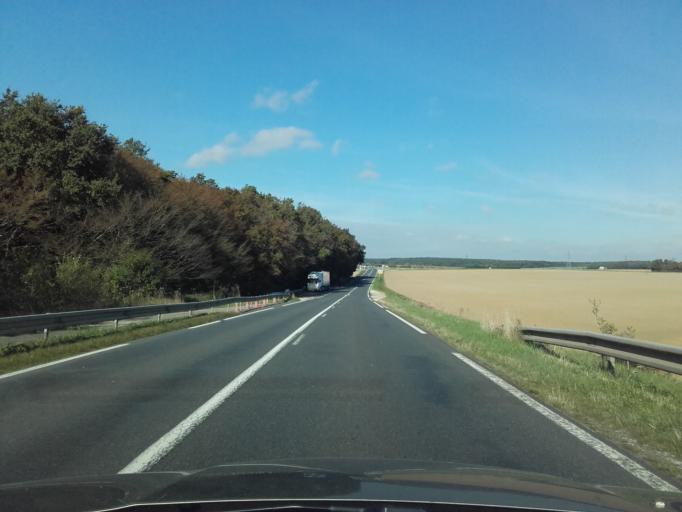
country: FR
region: Centre
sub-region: Departement d'Indre-et-Loire
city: Auzouer-en-Touraine
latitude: 47.5455
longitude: 0.9804
